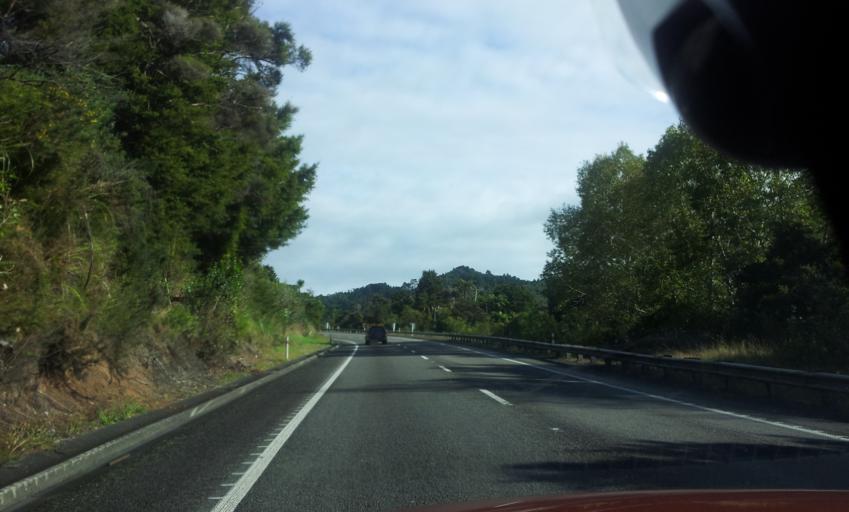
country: NZ
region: Auckland
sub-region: Auckland
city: Warkworth
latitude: -36.3699
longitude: 174.6263
